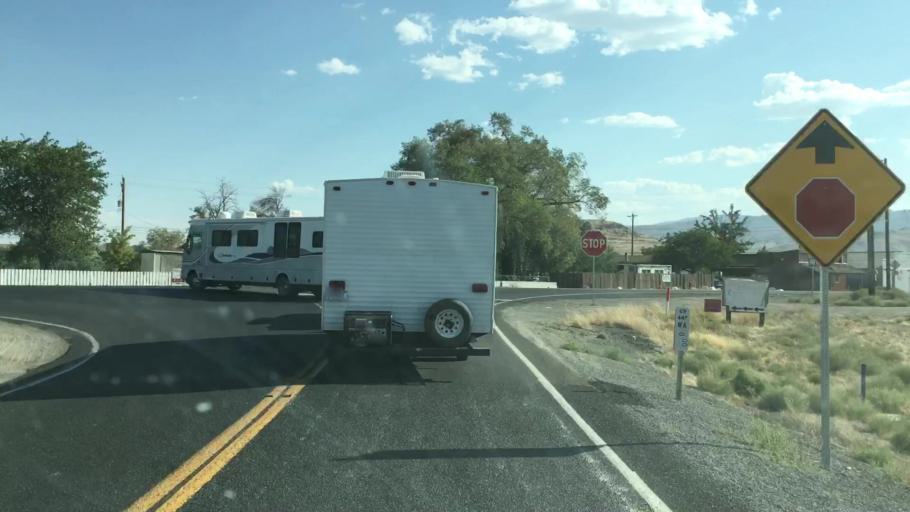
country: US
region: Nevada
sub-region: Lyon County
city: Fernley
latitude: 39.6309
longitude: -119.2906
